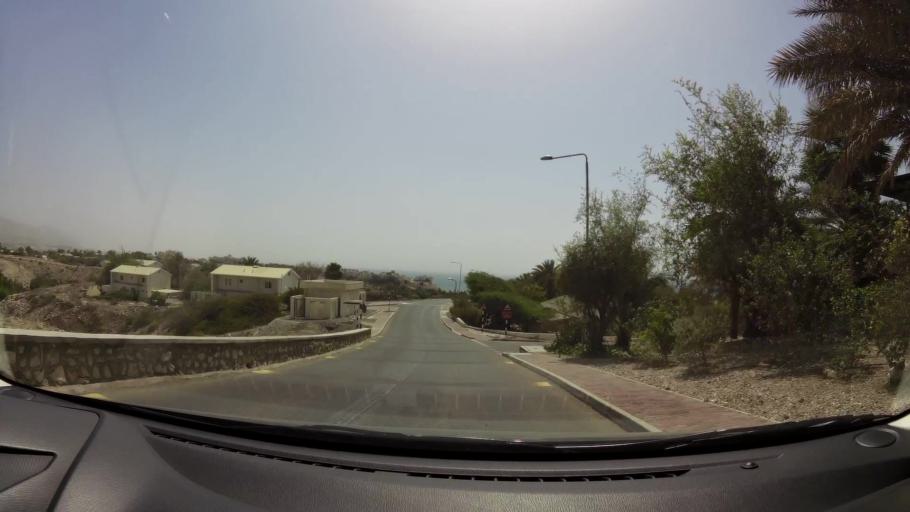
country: OM
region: Muhafazat Masqat
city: Muscat
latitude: 23.6340
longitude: 58.4952
